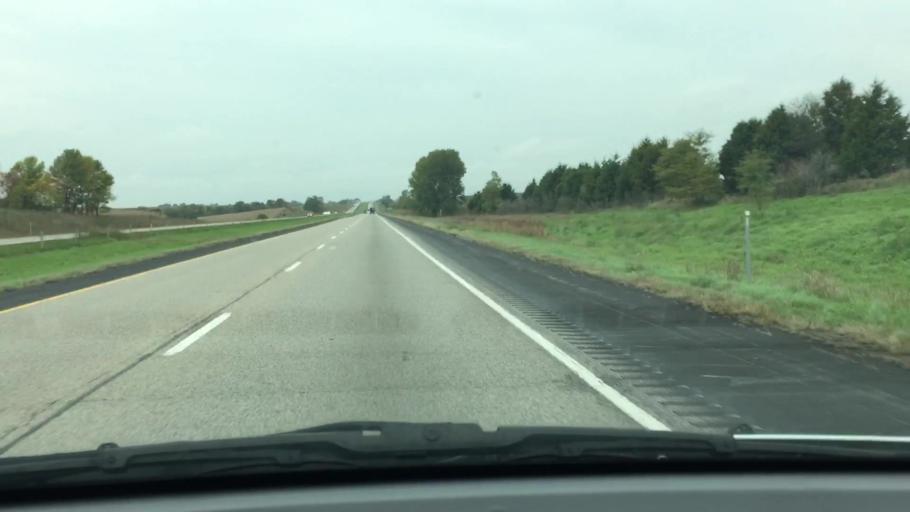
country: US
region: Iowa
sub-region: Muscatine County
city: West Liberty
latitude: 41.6601
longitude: -91.2155
